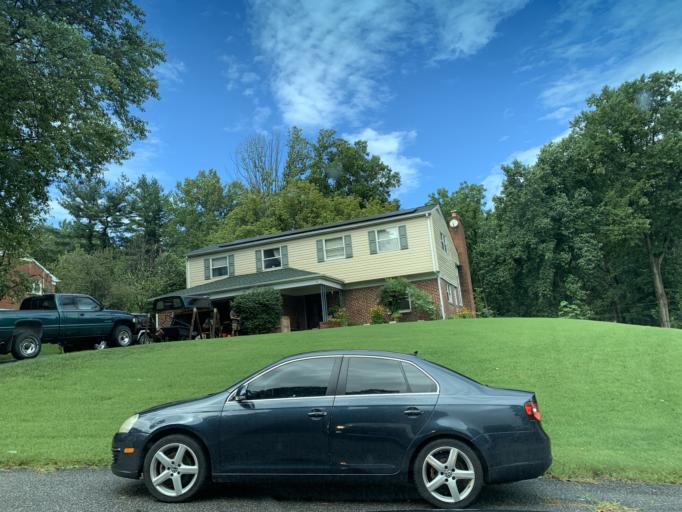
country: US
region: Maryland
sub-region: Baltimore County
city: Timonium
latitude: 39.4463
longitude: -76.6213
